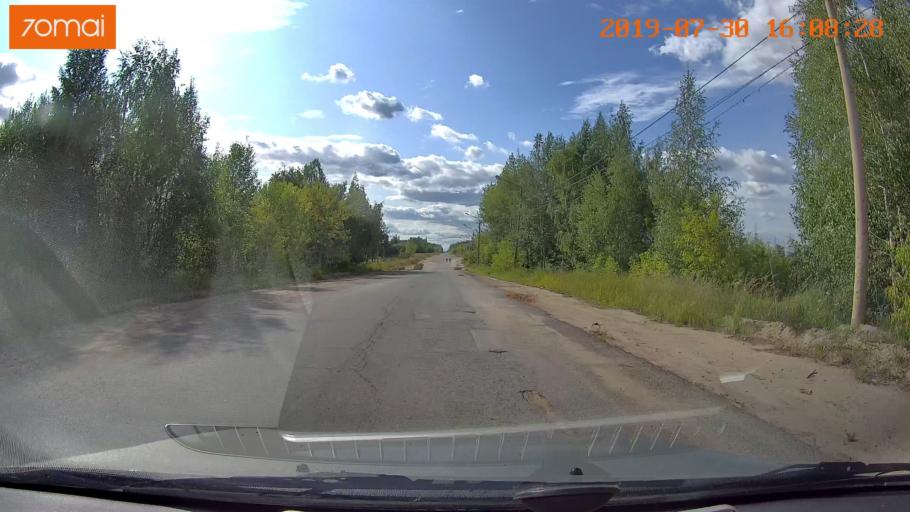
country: RU
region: Moskovskaya
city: Peski
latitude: 55.2483
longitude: 38.7232
